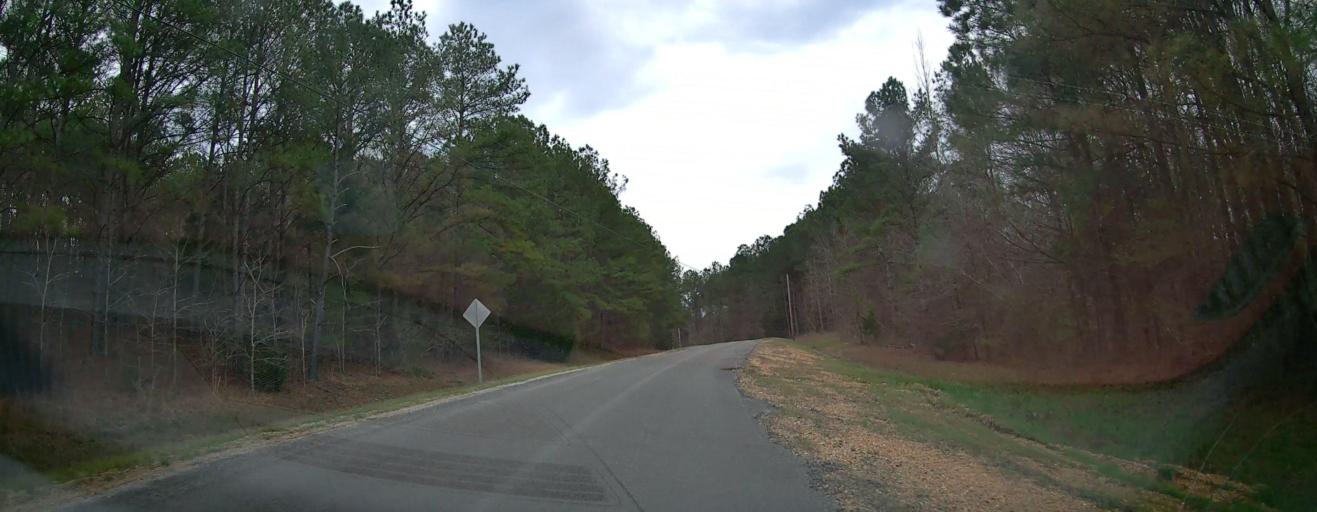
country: US
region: Mississippi
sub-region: Itawamba County
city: Fulton
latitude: 34.2148
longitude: -88.2083
